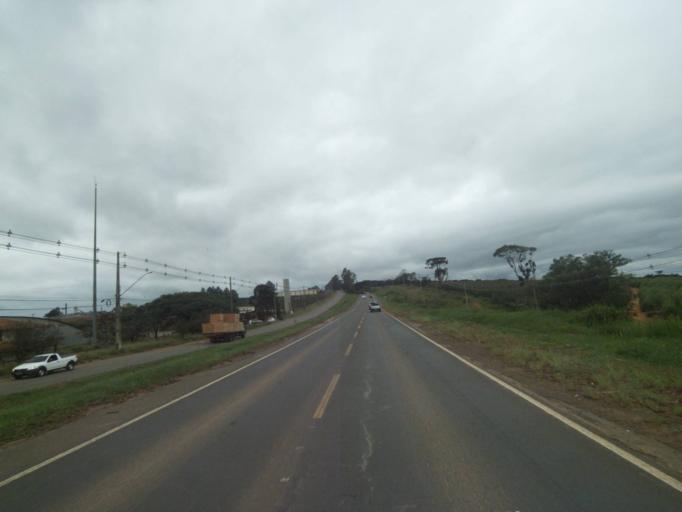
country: BR
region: Parana
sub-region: Telemaco Borba
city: Telemaco Borba
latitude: -24.3719
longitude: -50.6624
